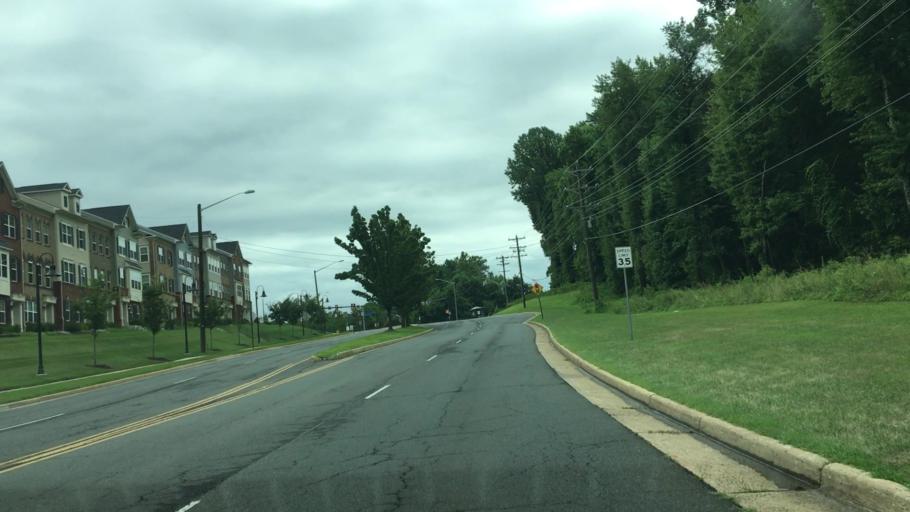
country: US
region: Virginia
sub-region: Prince William County
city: Buckhall
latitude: 38.7588
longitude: -77.4384
